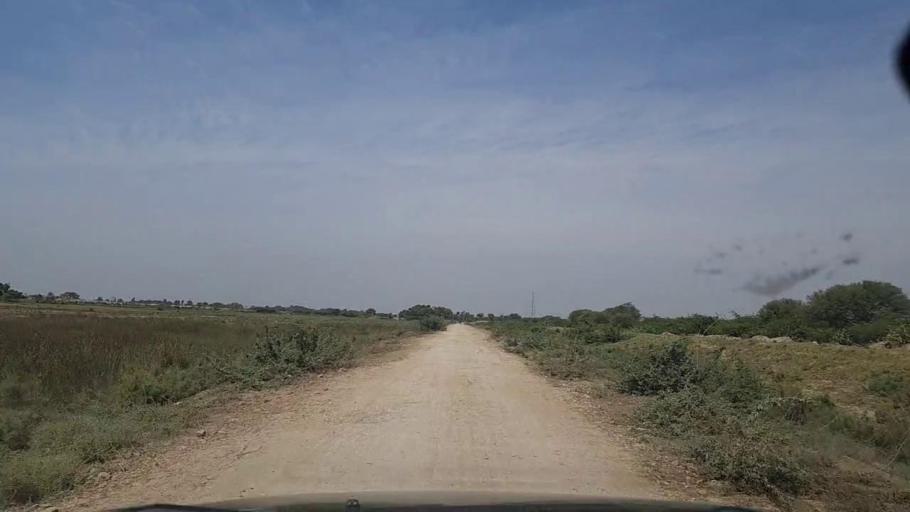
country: PK
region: Sindh
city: Mirpur Batoro
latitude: 24.6500
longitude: 68.1840
